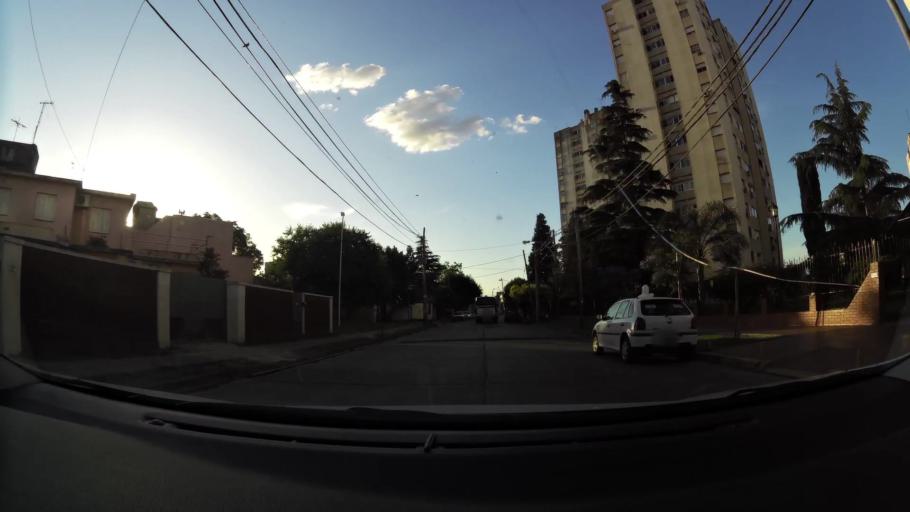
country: AR
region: Buenos Aires F.D.
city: Villa Lugano
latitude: -34.6938
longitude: -58.4794
